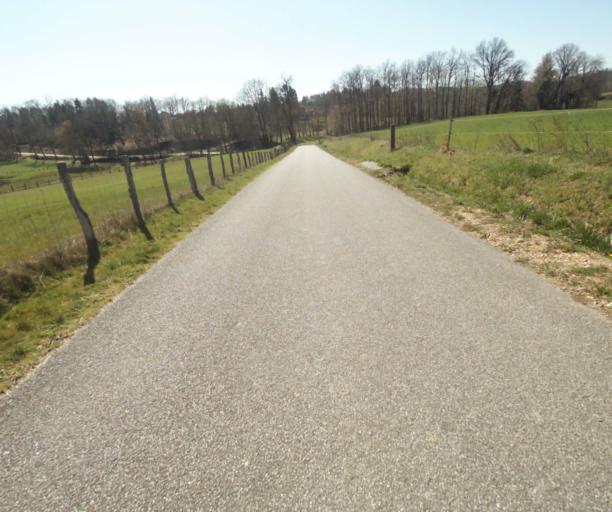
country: FR
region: Limousin
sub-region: Departement de la Correze
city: Saint-Mexant
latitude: 45.3100
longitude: 1.6473
